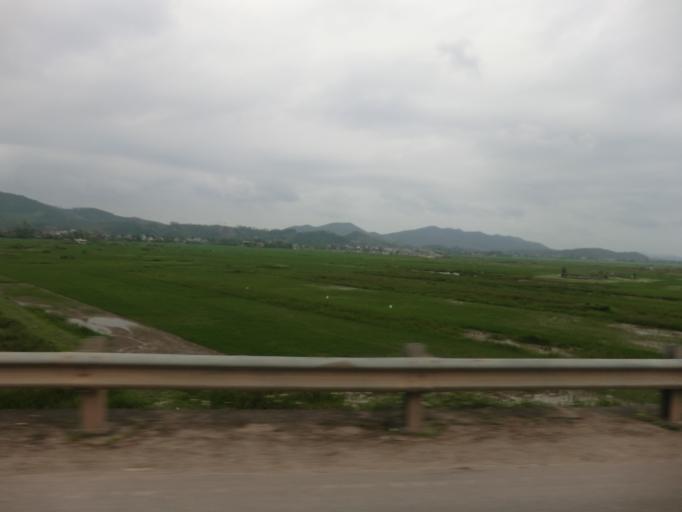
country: VN
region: Quang Binh
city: Ba Don
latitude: 17.6087
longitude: 106.3218
